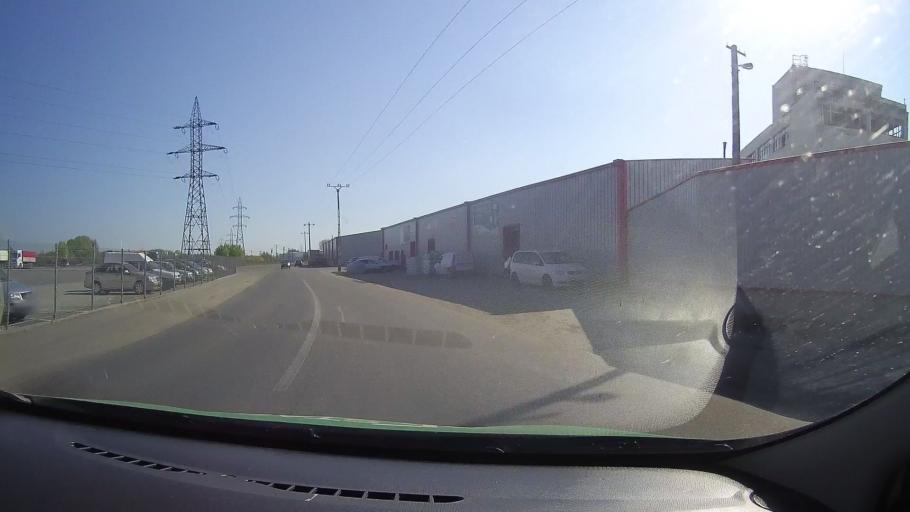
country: RO
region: Satu Mare
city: Carei
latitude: 47.6999
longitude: 22.4657
